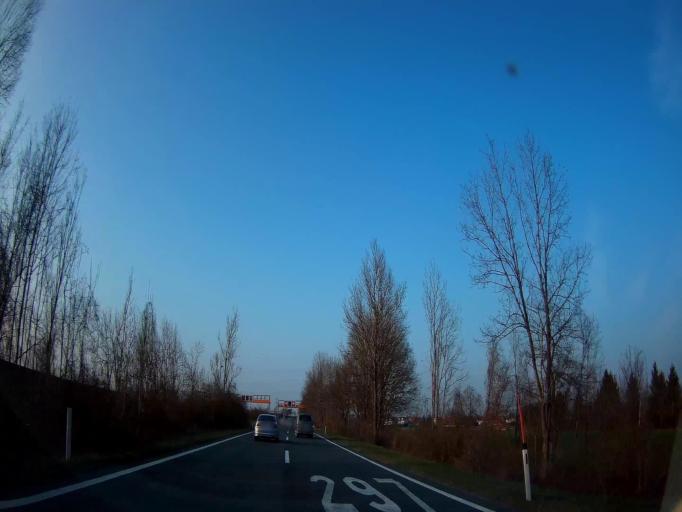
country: DE
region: Bavaria
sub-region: Upper Bavaria
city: Ainring
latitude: 47.7766
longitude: 12.9803
